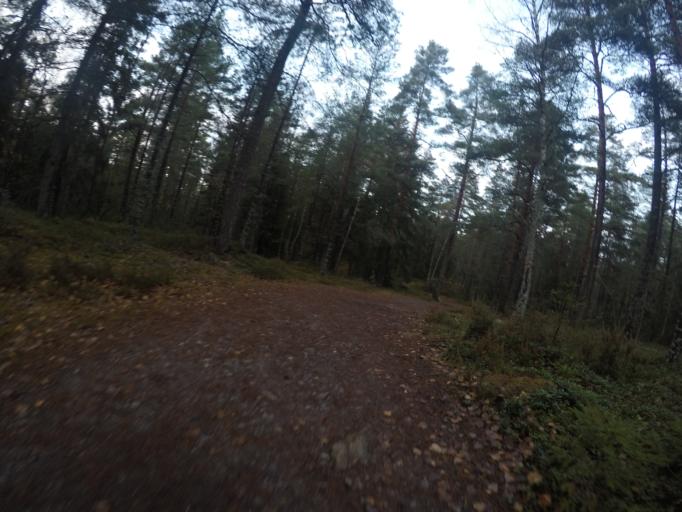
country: SE
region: Soedermanland
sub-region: Eskilstuna Kommun
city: Eskilstuna
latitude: 59.3442
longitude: 16.5196
